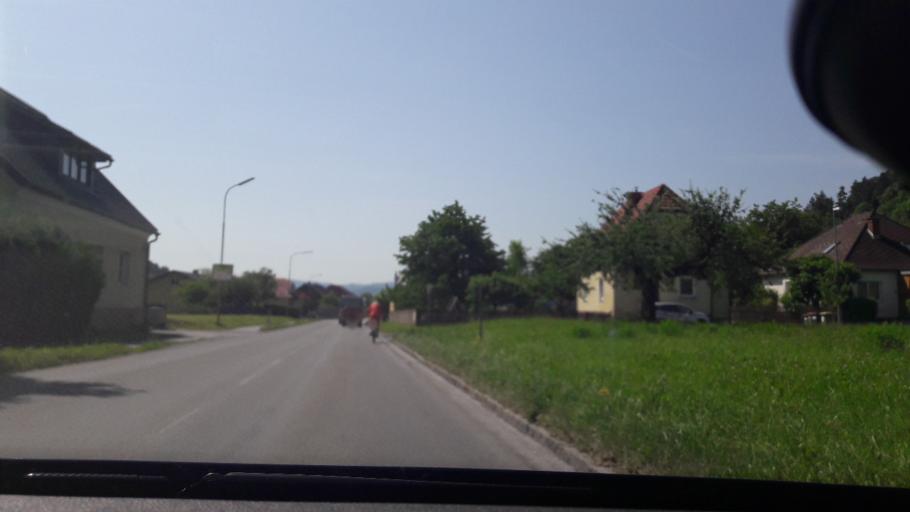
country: AT
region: Styria
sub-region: Politischer Bezirk Voitsberg
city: Kohlschwarz
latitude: 47.0901
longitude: 15.1218
